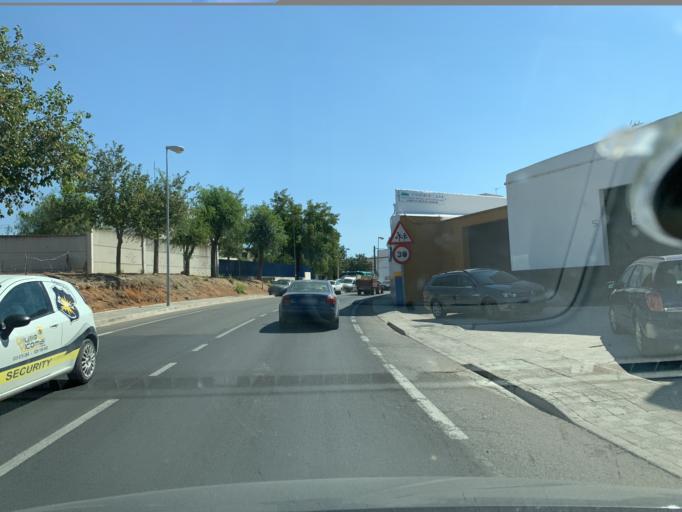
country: ES
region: Andalusia
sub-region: Provincia de Sevilla
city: Marchena
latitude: 37.3309
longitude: -5.4107
